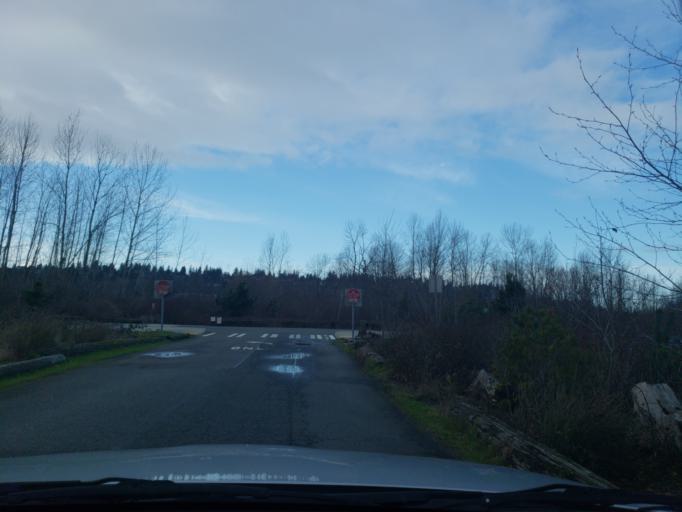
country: US
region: Washington
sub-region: King County
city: Kirkland
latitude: 47.6773
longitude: -122.2520
